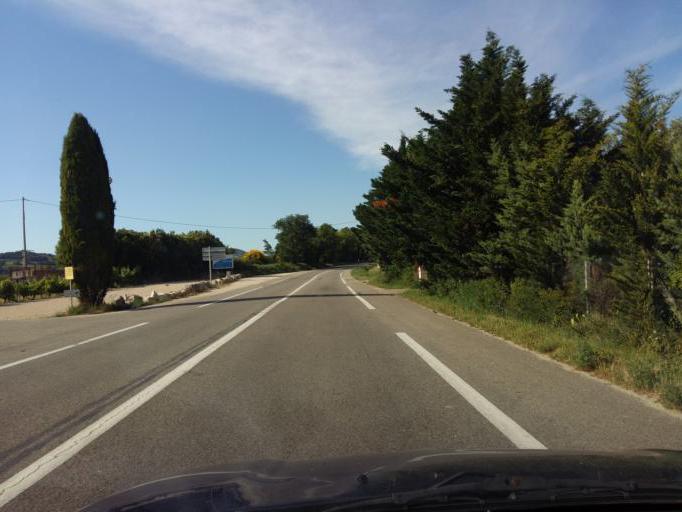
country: FR
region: Provence-Alpes-Cote d'Azur
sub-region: Departement du Vaucluse
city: Sablet
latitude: 44.2219
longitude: 5.0080
